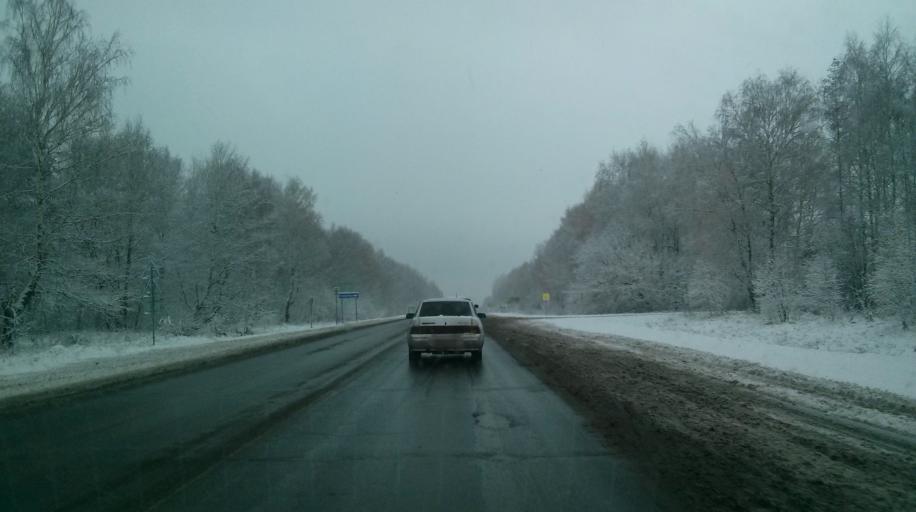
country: RU
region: Nizjnij Novgorod
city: Burevestnik
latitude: 56.1568
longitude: 43.7072
